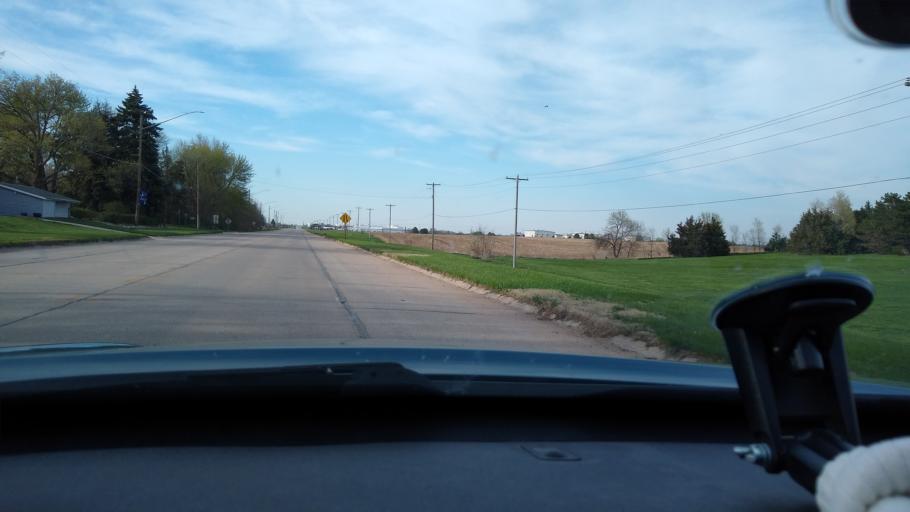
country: US
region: Nebraska
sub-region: Fillmore County
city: Geneva
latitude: 40.5324
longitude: -97.5958
